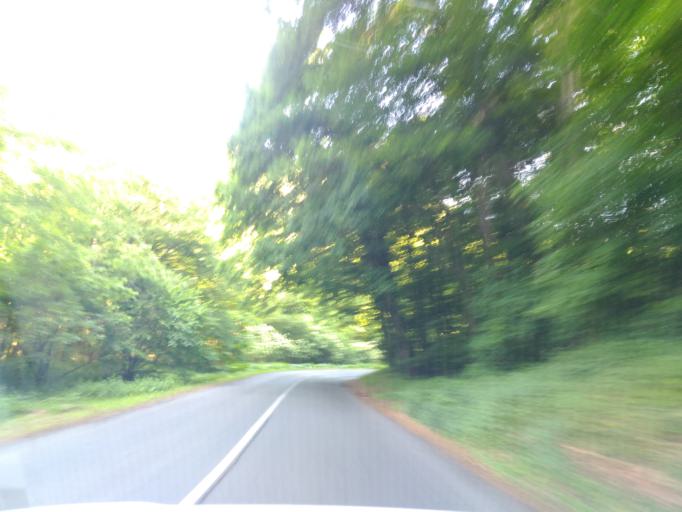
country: HU
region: Baranya
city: Komlo
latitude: 46.2078
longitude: 18.3006
